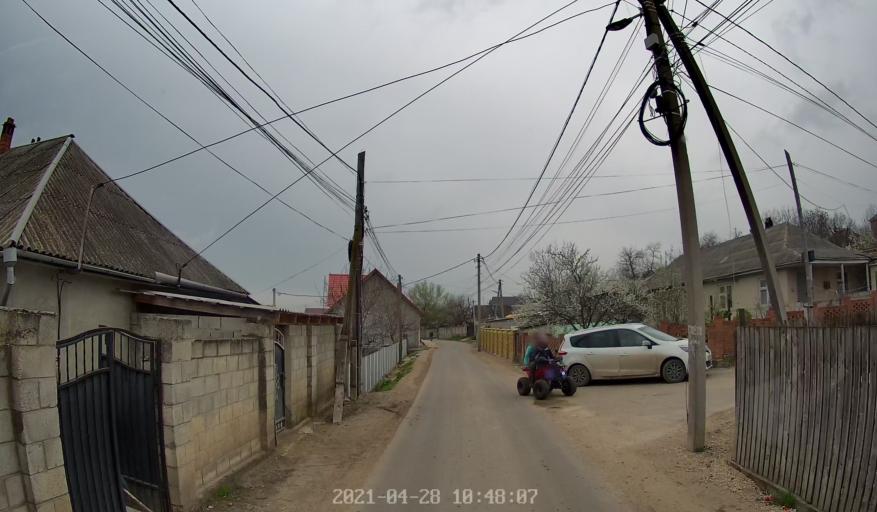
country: MD
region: Chisinau
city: Singera
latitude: 46.9859
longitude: 28.9454
